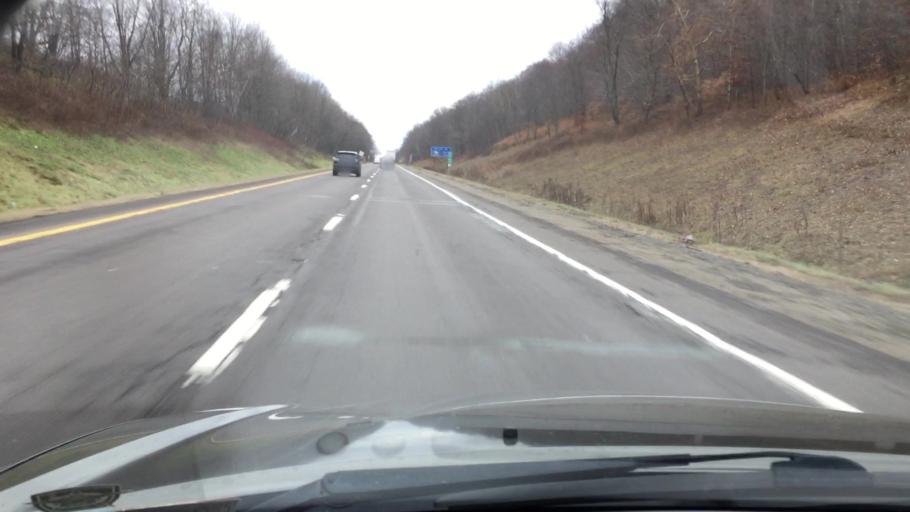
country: US
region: Pennsylvania
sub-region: Luzerne County
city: White Haven
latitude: 41.0572
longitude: -75.7298
